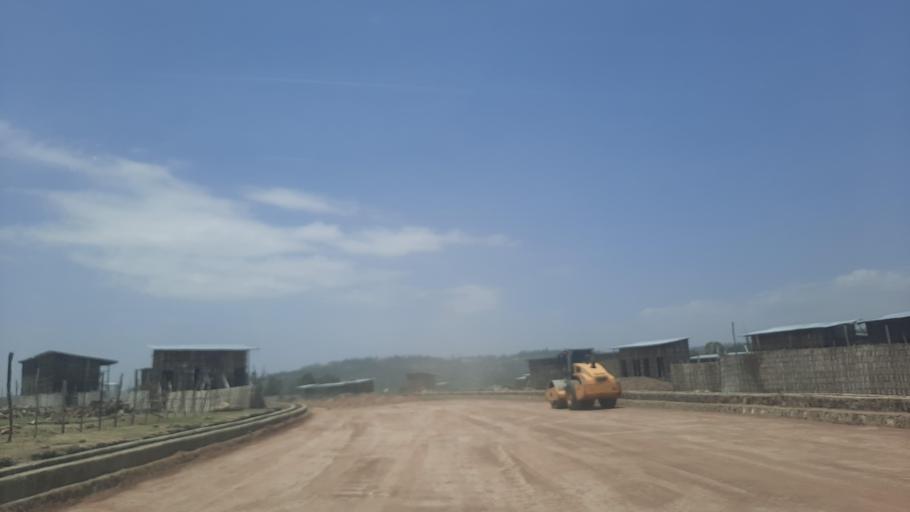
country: ET
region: Southern Nations, Nationalities, and People's Region
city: Butajira
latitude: 7.8447
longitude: 38.1728
